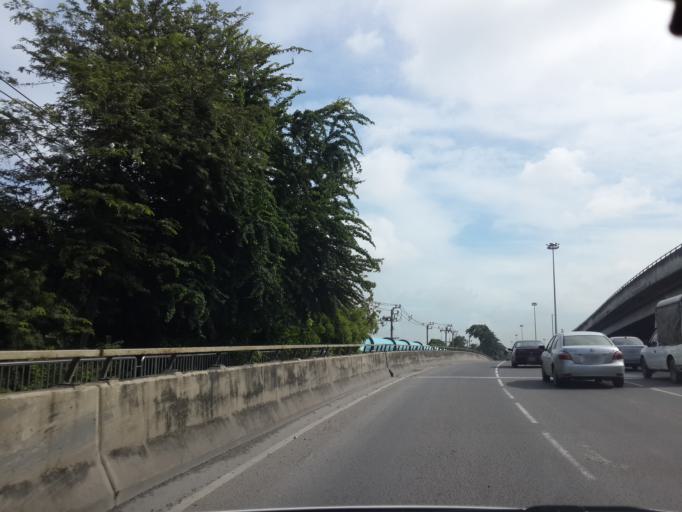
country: TH
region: Bangkok
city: Huai Khwang
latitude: 13.7596
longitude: 100.5957
